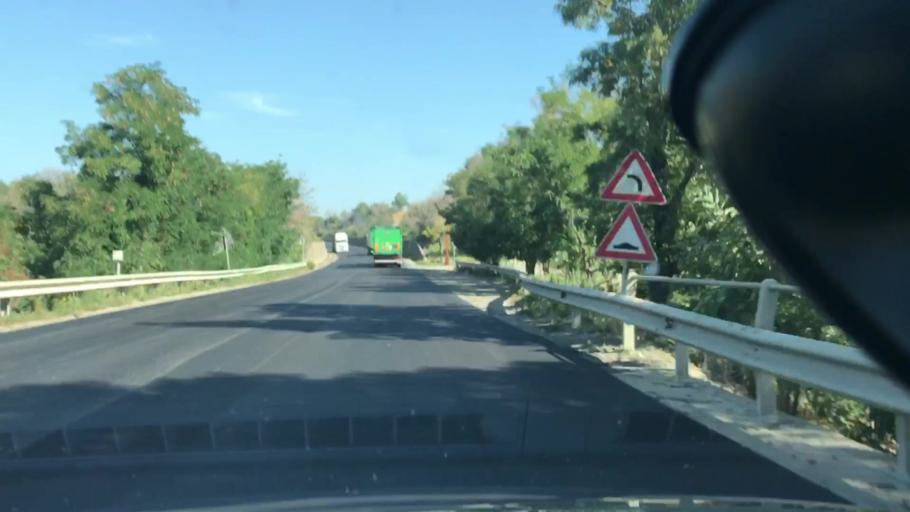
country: IT
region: Apulia
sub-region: Provincia di Foggia
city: Candela
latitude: 41.0983
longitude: 15.5942
